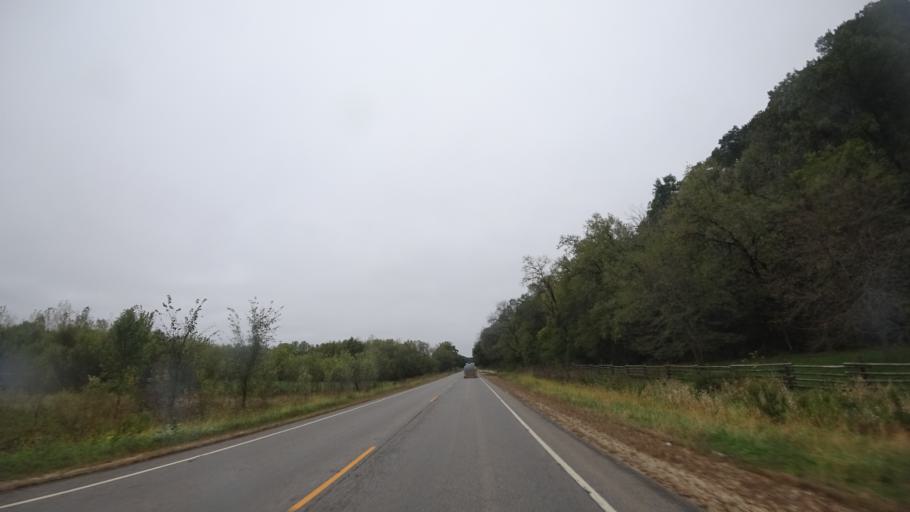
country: US
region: Wisconsin
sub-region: Crawford County
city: Prairie du Chien
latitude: 43.0587
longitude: -90.9603
